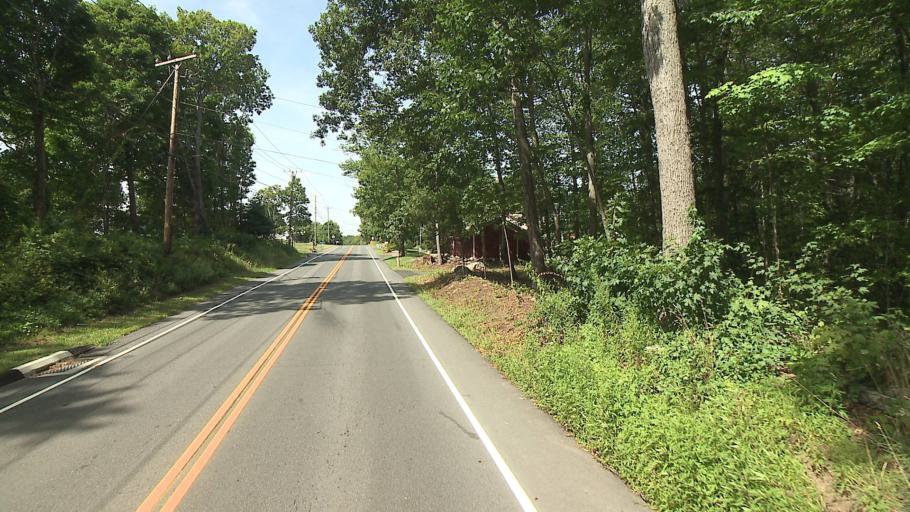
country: US
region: Connecticut
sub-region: Litchfield County
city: Bethlehem Village
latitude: 41.6124
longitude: -73.1825
